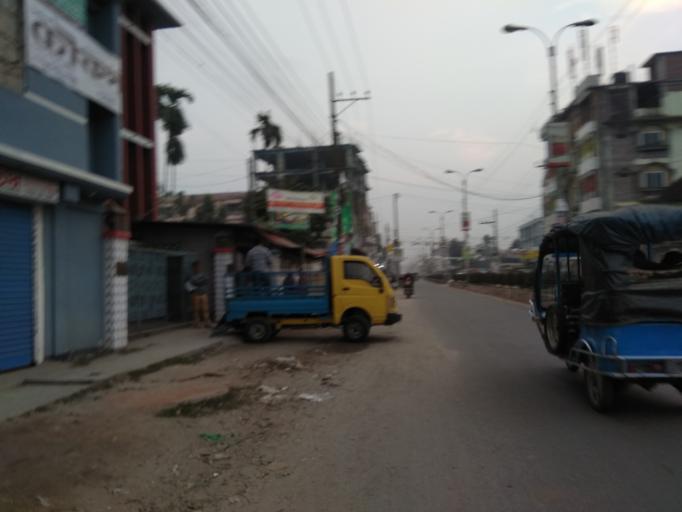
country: BD
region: Rangpur Division
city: Rangpur
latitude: 25.7332
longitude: 89.2548
